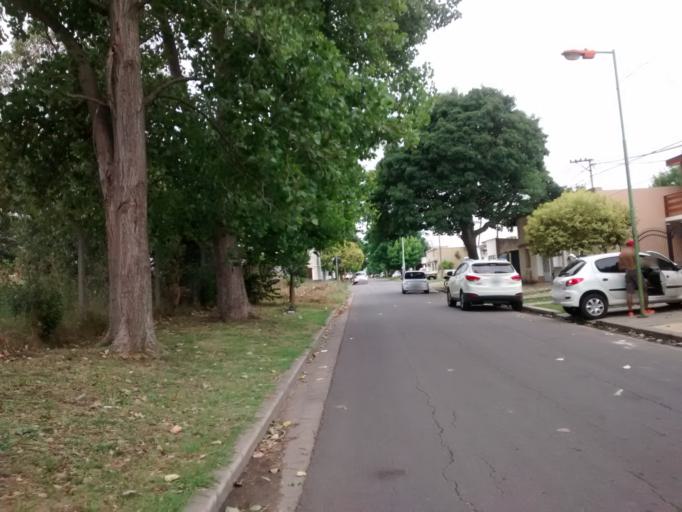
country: AR
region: Buenos Aires
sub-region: Partido de La Plata
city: La Plata
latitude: -34.9383
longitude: -57.9239
